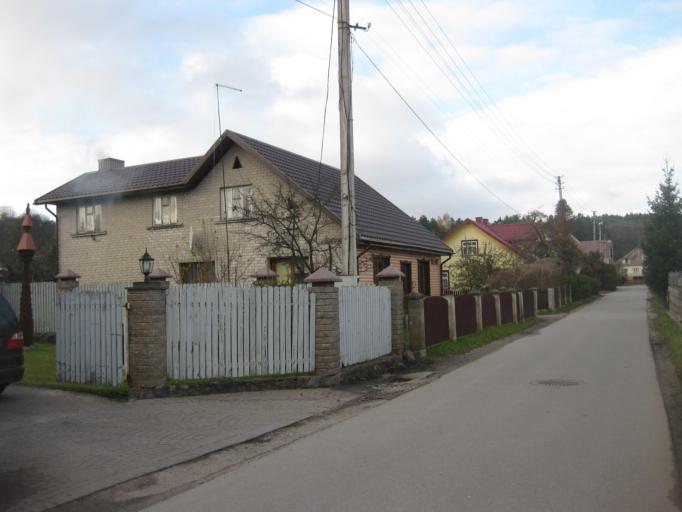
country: LT
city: Prienai
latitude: 54.6401
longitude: 23.9461
